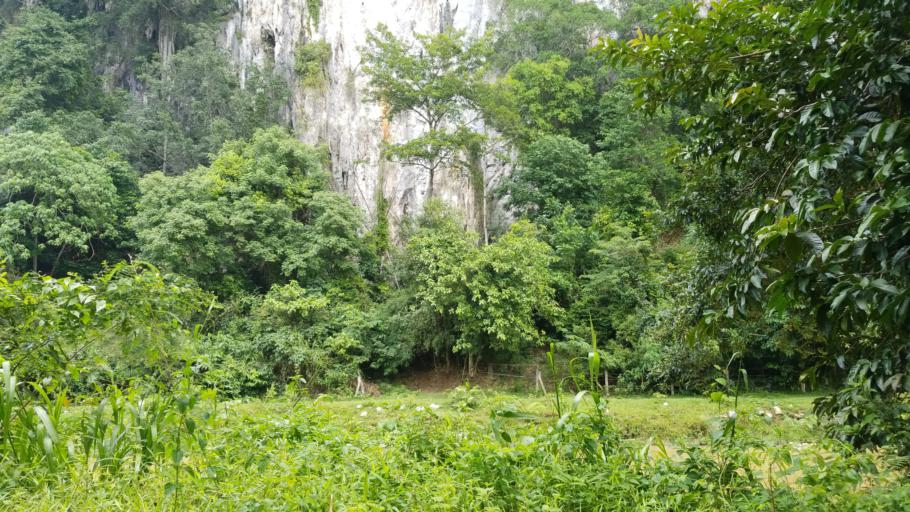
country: TH
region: Yala
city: Betong
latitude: 5.6708
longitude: 100.9087
